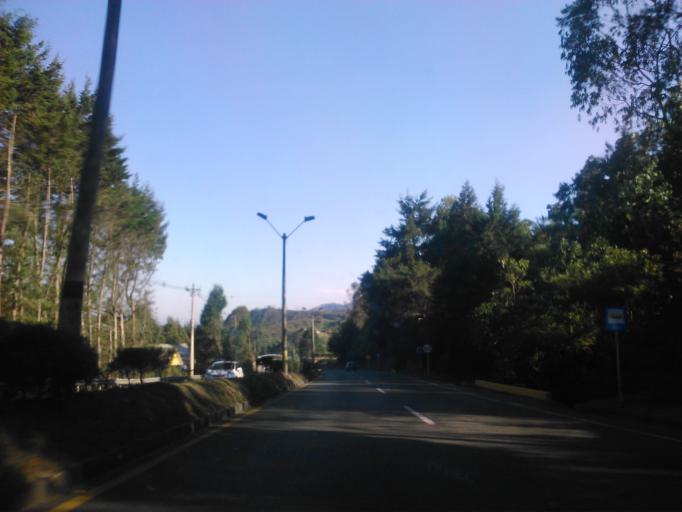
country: CO
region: Antioquia
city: Guarne
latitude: 6.3111
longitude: -75.4606
